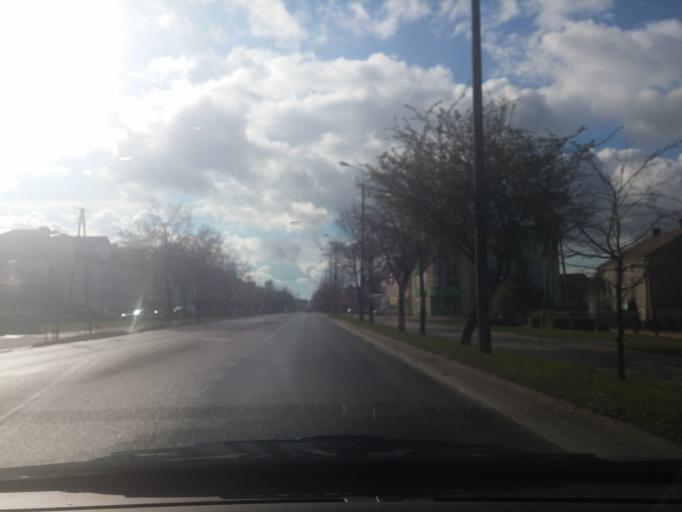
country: PL
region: Masovian Voivodeship
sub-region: Siedlce
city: Siedlce
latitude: 52.1687
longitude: 22.2417
